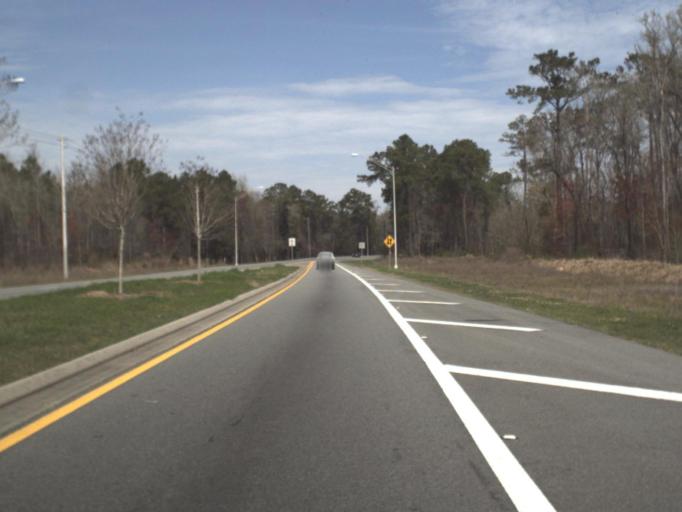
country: US
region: Florida
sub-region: Gadsden County
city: Midway
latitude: 30.4857
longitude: -84.3631
